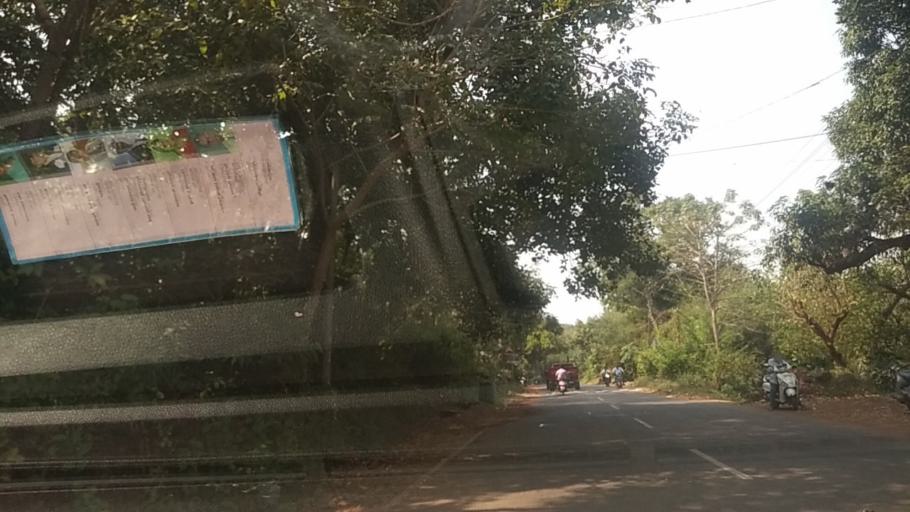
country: IN
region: Goa
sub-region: North Goa
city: Morjim
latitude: 15.6607
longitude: 73.7410
